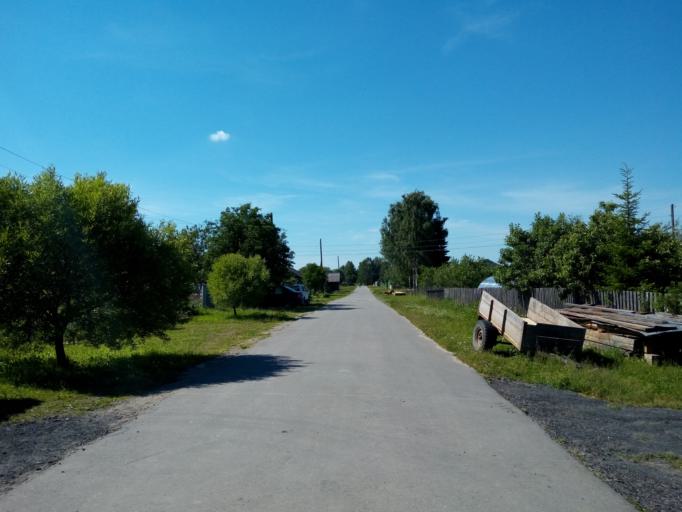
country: RU
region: Nizjnij Novgorod
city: Voskresenskoye
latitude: 56.7812
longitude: 45.5188
